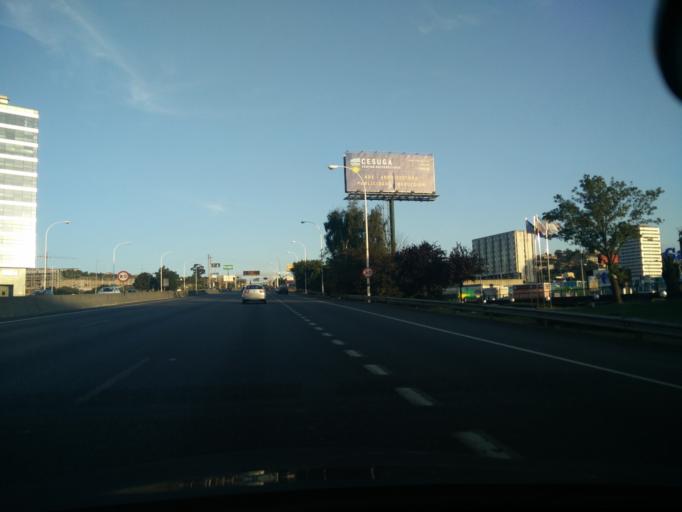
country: ES
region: Galicia
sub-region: Provincia da Coruna
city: A Coruna
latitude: 43.3404
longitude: -8.4070
